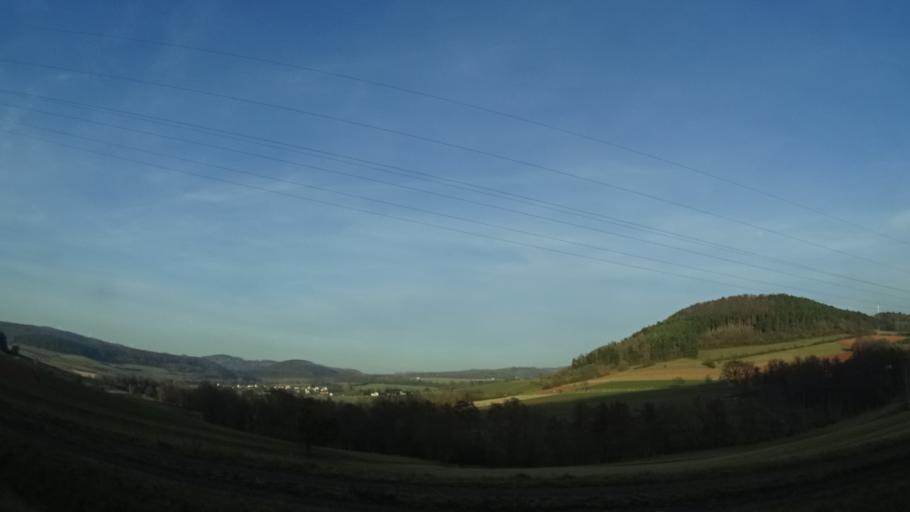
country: DE
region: Hesse
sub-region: Regierungsbezirk Darmstadt
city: Schluchtern
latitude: 50.3298
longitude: 9.5850
